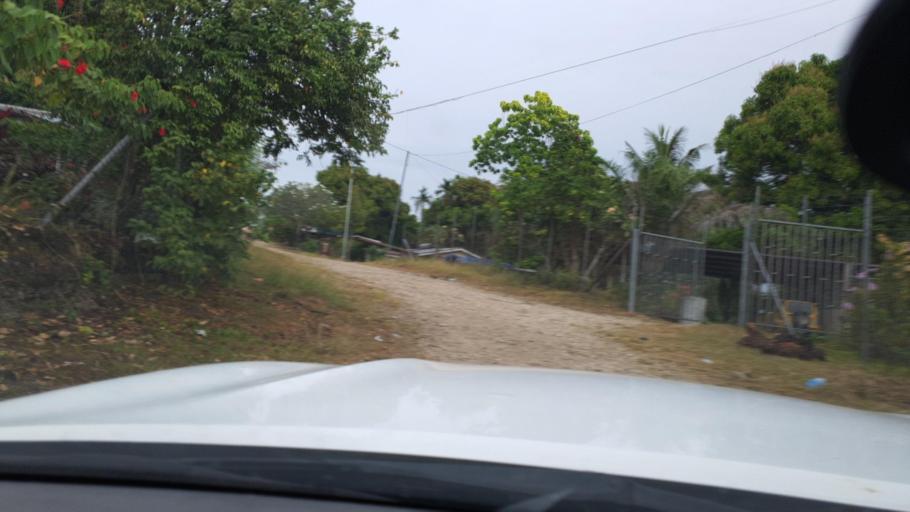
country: SB
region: Guadalcanal
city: Honiara
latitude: -9.4424
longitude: 159.9638
